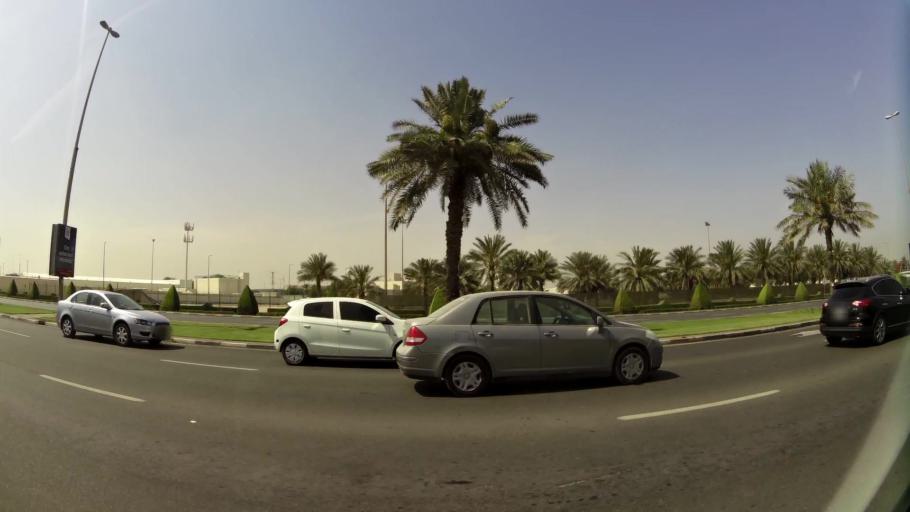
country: AE
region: Ash Shariqah
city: Sharjah
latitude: 25.2679
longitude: 55.3617
